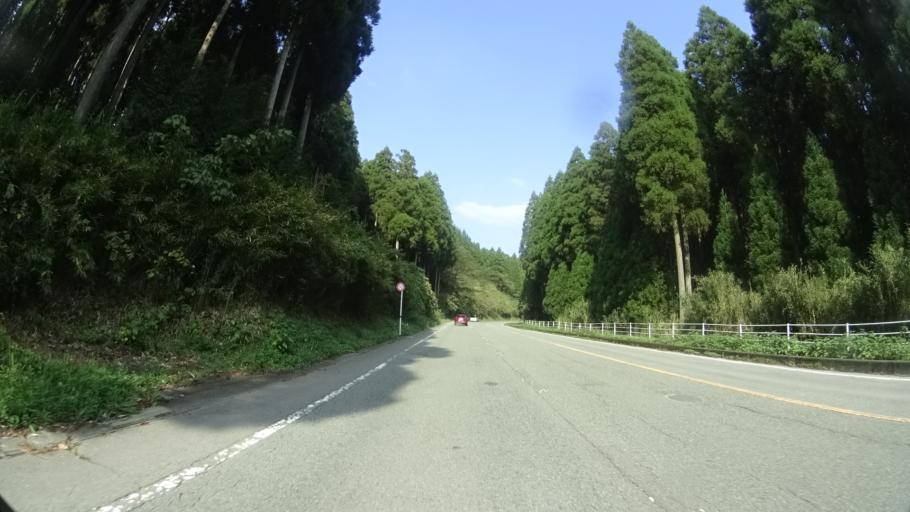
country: JP
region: Oita
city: Tsukawaki
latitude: 33.1247
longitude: 131.0729
